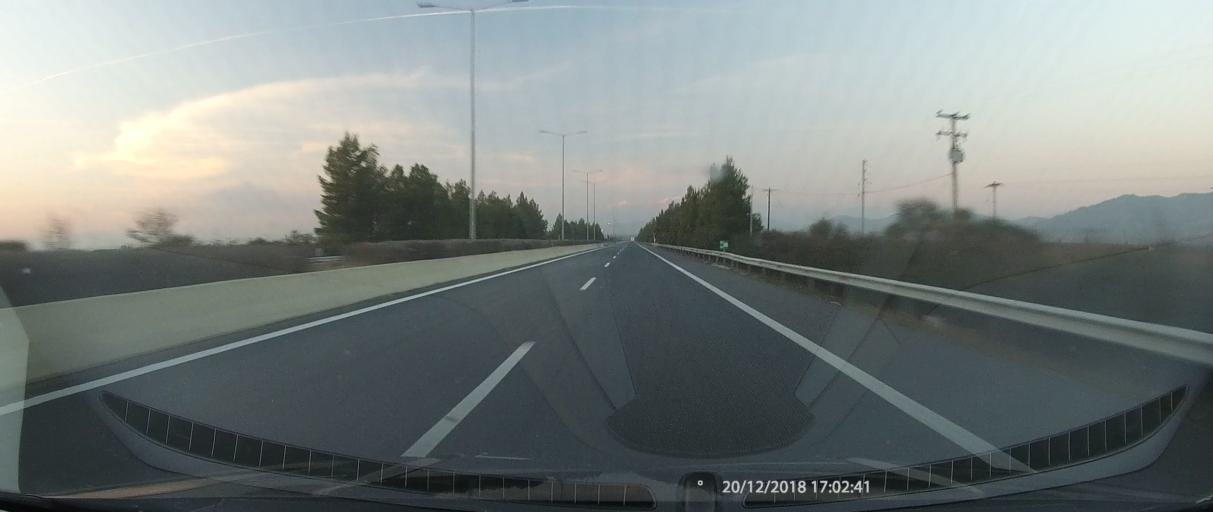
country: GR
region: Thessaly
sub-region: Nomos Larisis
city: Platykampos
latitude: 39.6812
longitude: 22.4954
